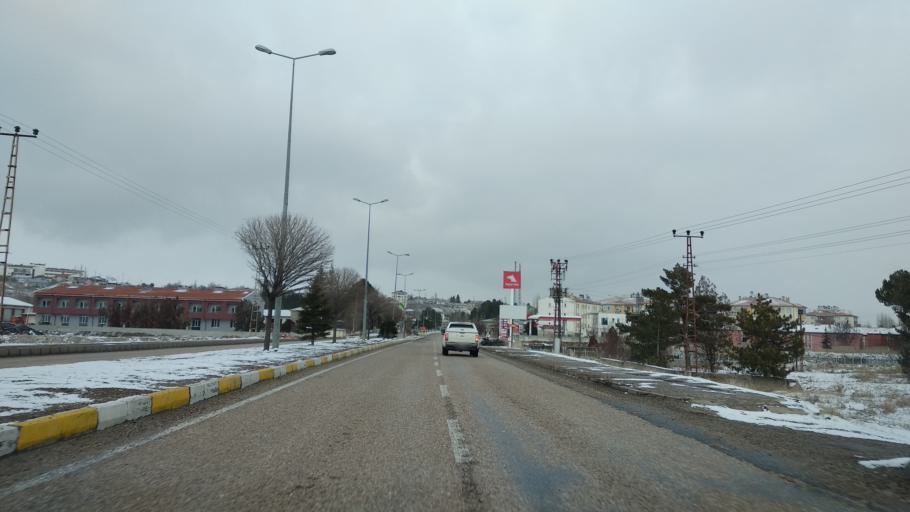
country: TR
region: Kayseri
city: Pinarbasi
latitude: 38.7184
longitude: 36.3844
